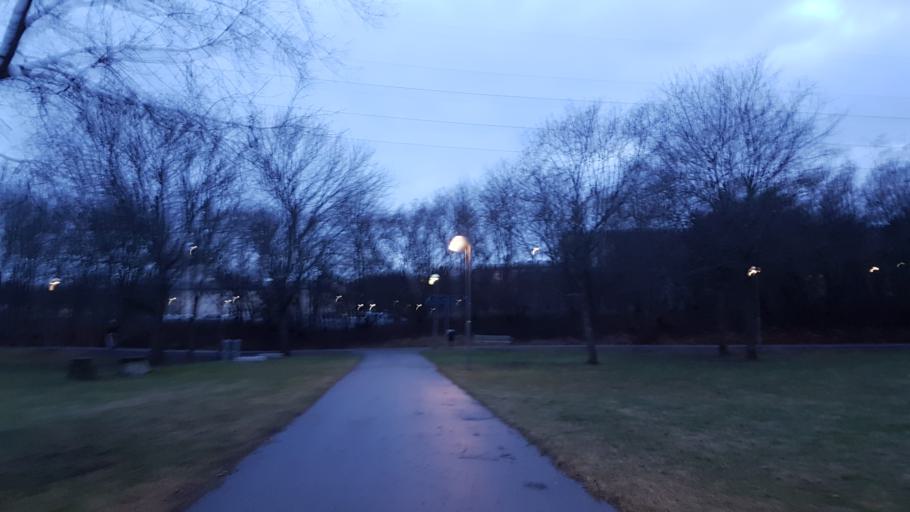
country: SE
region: Stockholm
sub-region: Stockholms Kommun
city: Arsta
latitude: 59.2715
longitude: 18.0537
